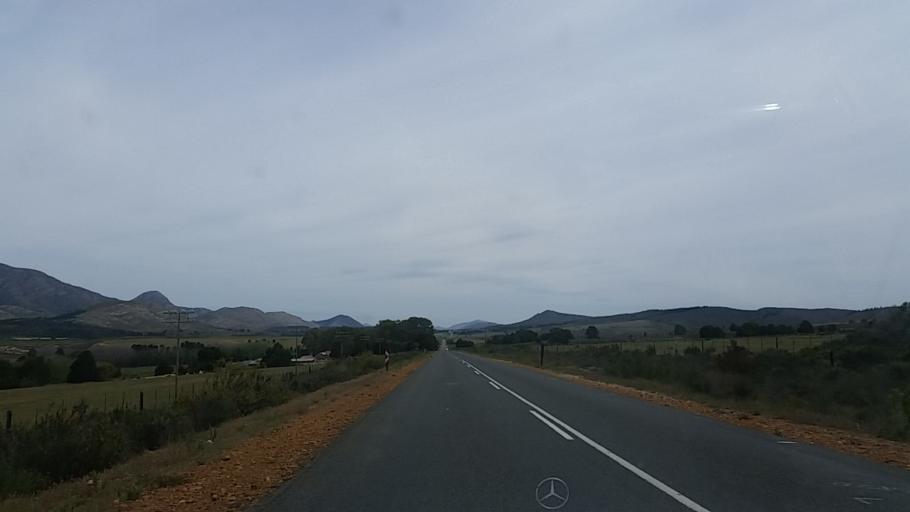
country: ZA
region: Western Cape
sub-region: Eden District Municipality
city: Knysna
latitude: -33.7608
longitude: 22.8549
